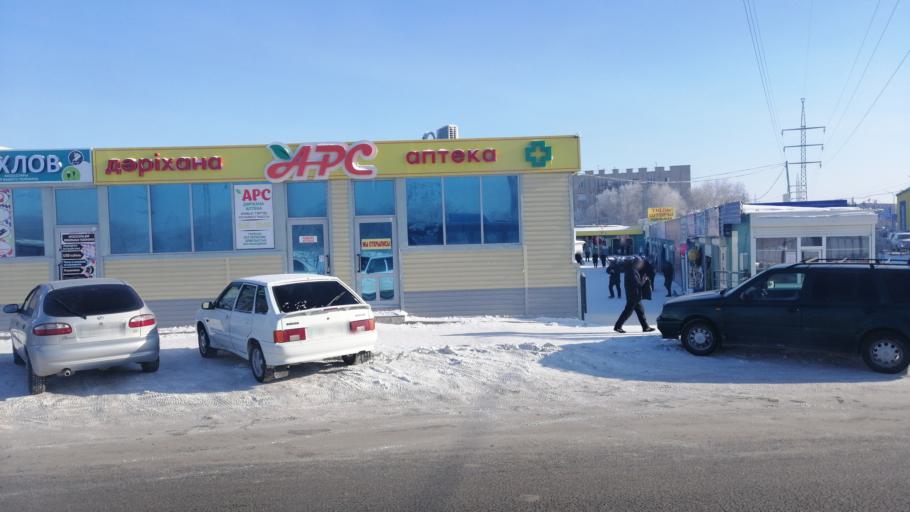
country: KZ
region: Aqtoebe
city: Aqtobe
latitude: 50.2959
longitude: 57.1978
